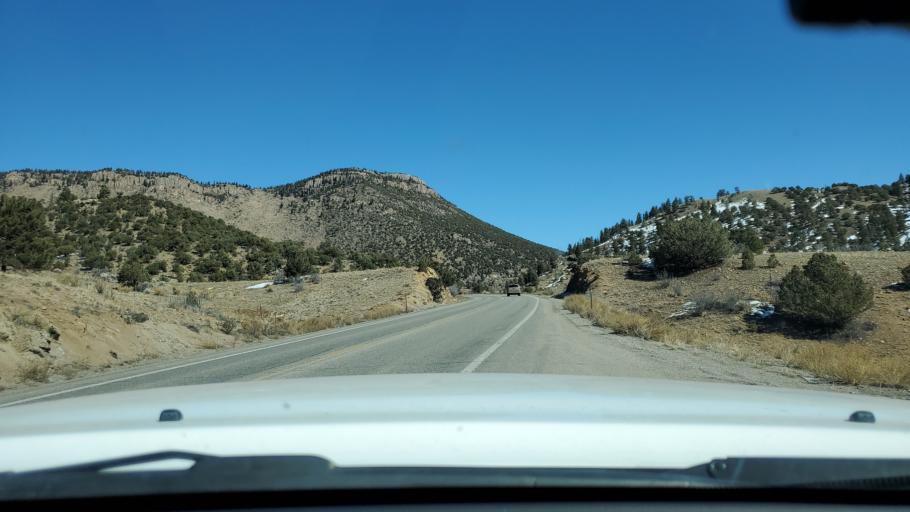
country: US
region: Colorado
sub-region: Chaffee County
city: Buena Vista
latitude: 38.8359
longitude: -106.0199
